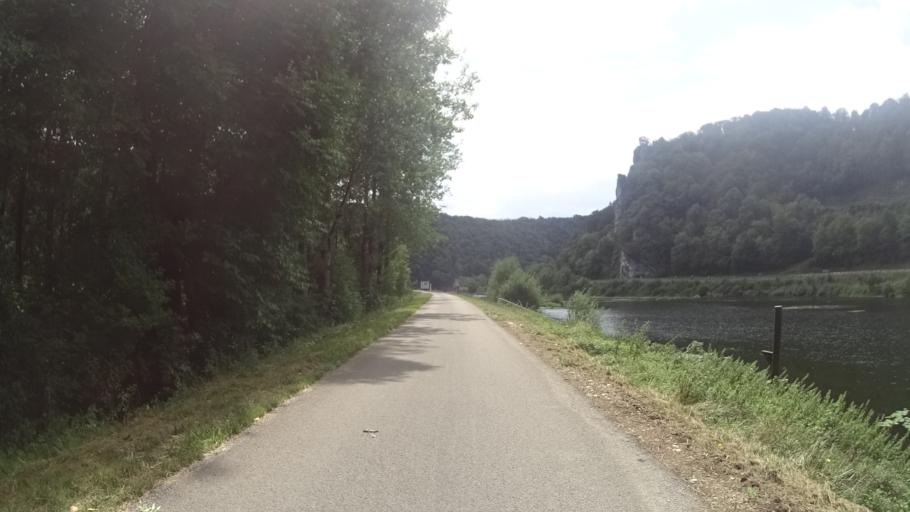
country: FR
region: Franche-Comte
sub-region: Departement du Doubs
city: Baume-les-Dames
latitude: 47.3654
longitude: 6.4190
